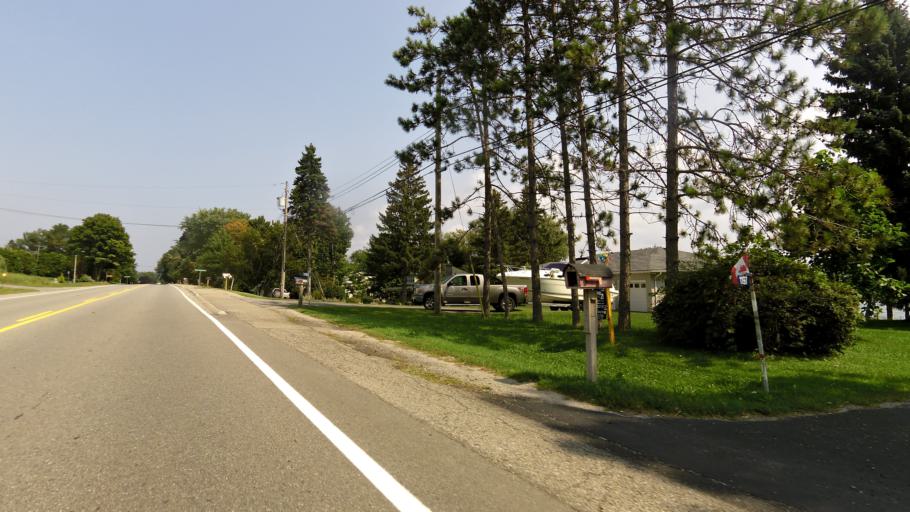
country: CA
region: Ontario
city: Brockville
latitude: 44.6281
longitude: -75.6236
